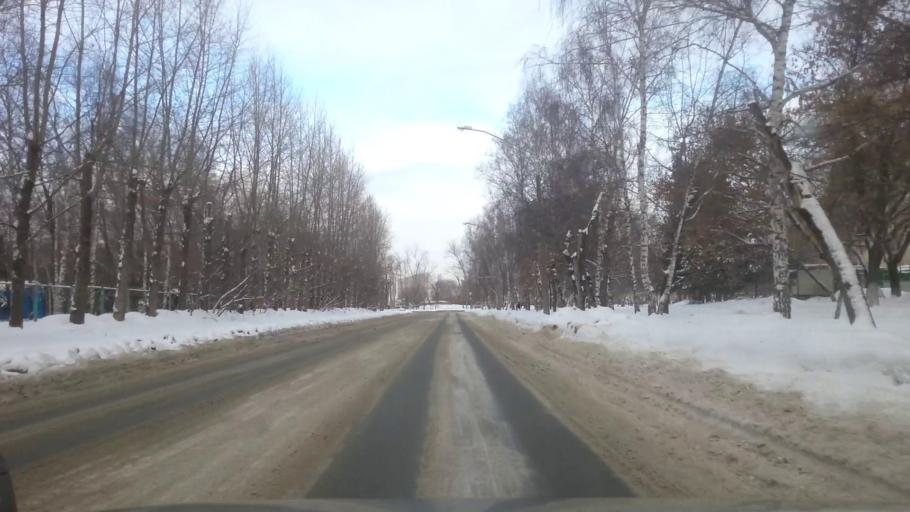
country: RU
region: Altai Krai
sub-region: Gorod Barnaulskiy
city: Barnaul
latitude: 53.3683
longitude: 83.6936
